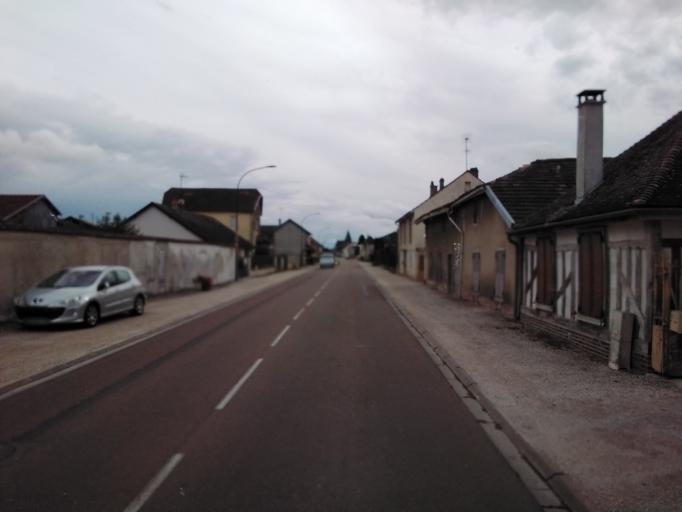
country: FR
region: Champagne-Ardenne
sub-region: Departement de l'Aube
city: Brienne-le-Chateau
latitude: 48.3785
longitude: 4.5296
